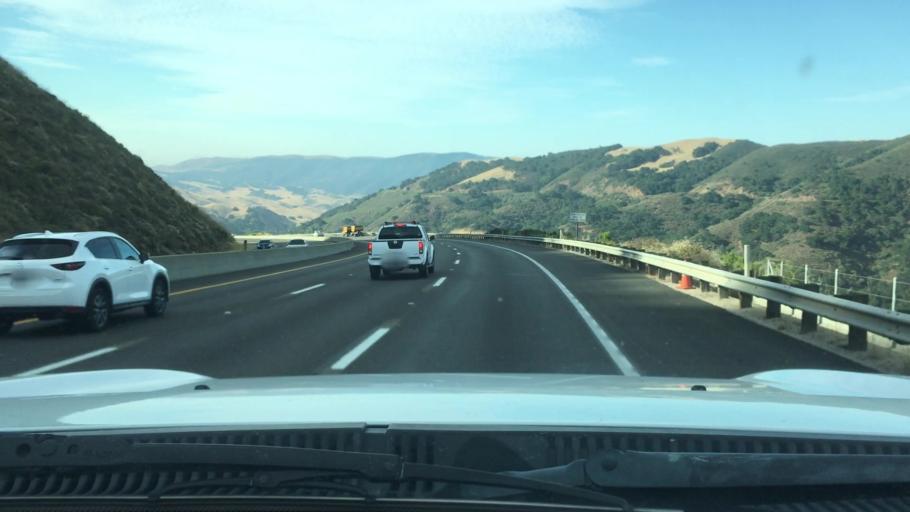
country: US
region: California
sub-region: San Luis Obispo County
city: Santa Margarita
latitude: 35.3400
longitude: -120.6281
